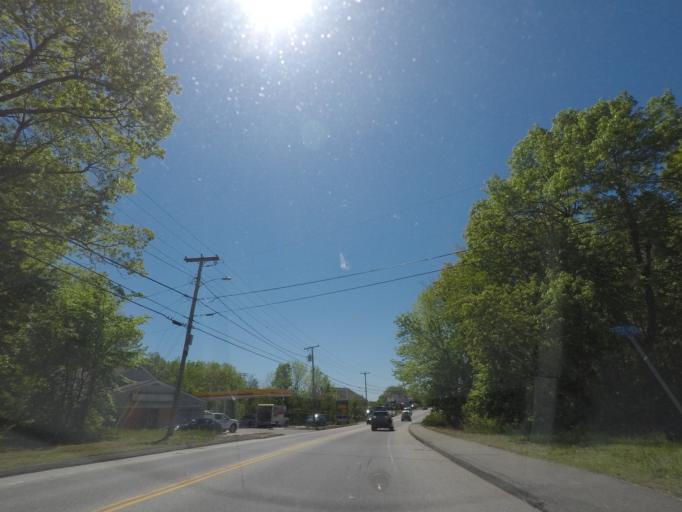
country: US
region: Maine
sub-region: Kennebec County
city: Farmingdale
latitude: 44.2568
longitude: -69.7735
